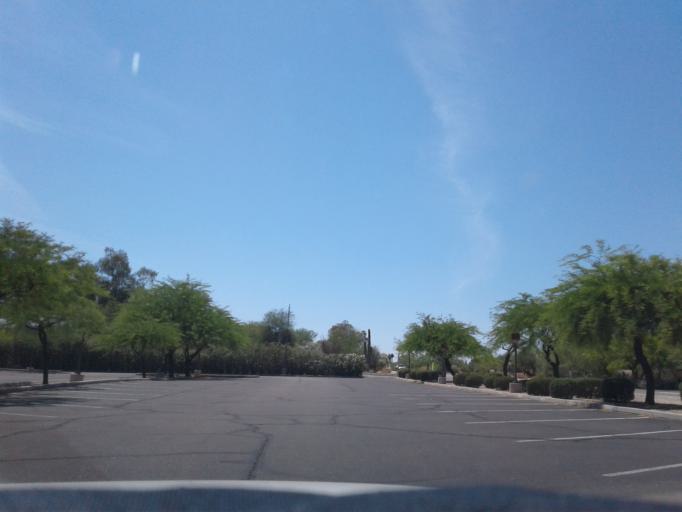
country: US
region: Arizona
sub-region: Maricopa County
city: Paradise Valley
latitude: 33.5171
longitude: -111.9987
